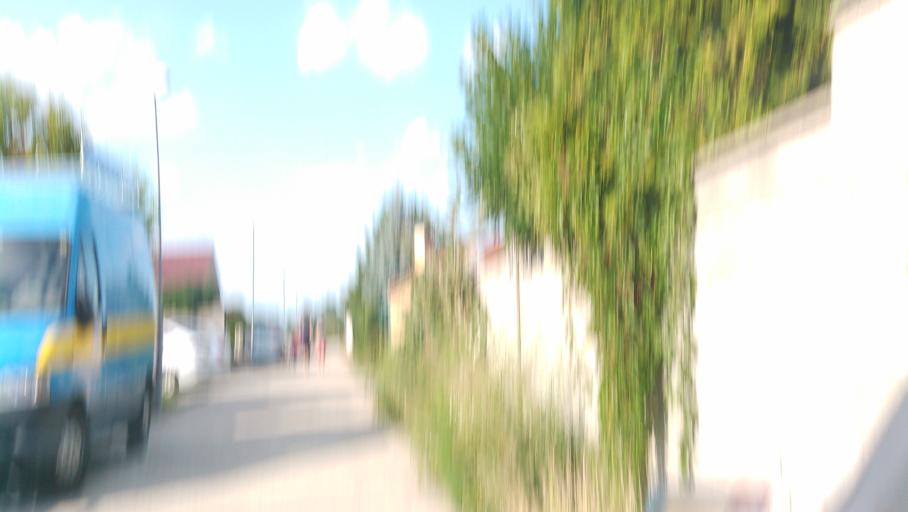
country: SK
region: Bratislavsky
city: Dunajska Luzna
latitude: 48.1716
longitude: 17.2806
